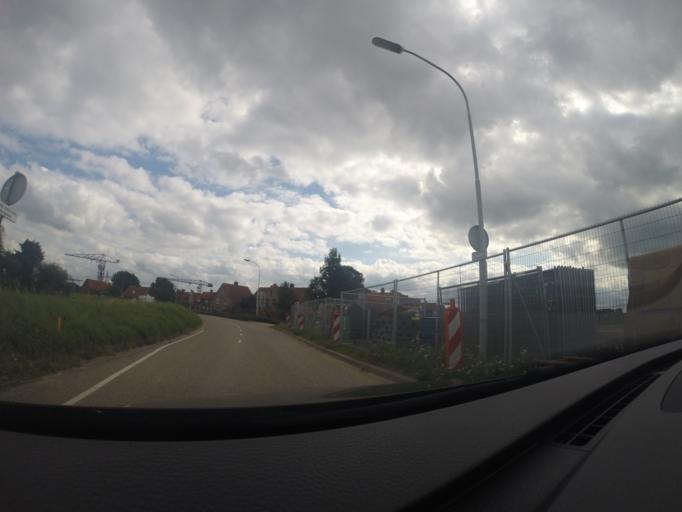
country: NL
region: Gelderland
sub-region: Gemeente Zevenaar
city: Zevenaar
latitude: 51.8563
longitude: 6.0938
